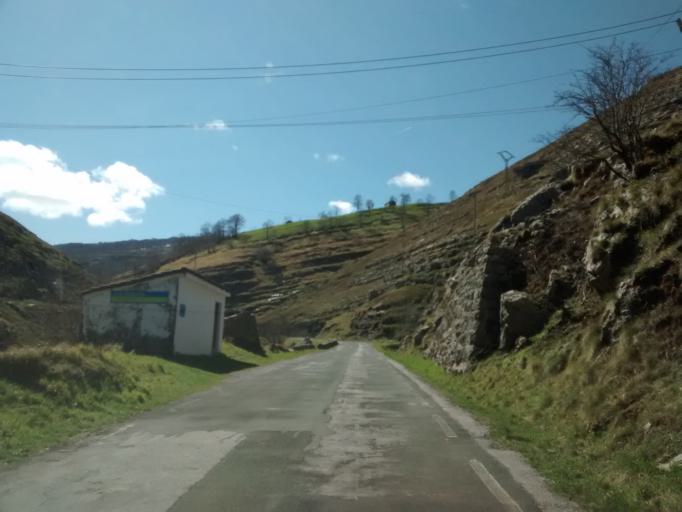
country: ES
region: Cantabria
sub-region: Provincia de Cantabria
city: Selaya
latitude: 43.2230
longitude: -3.7076
